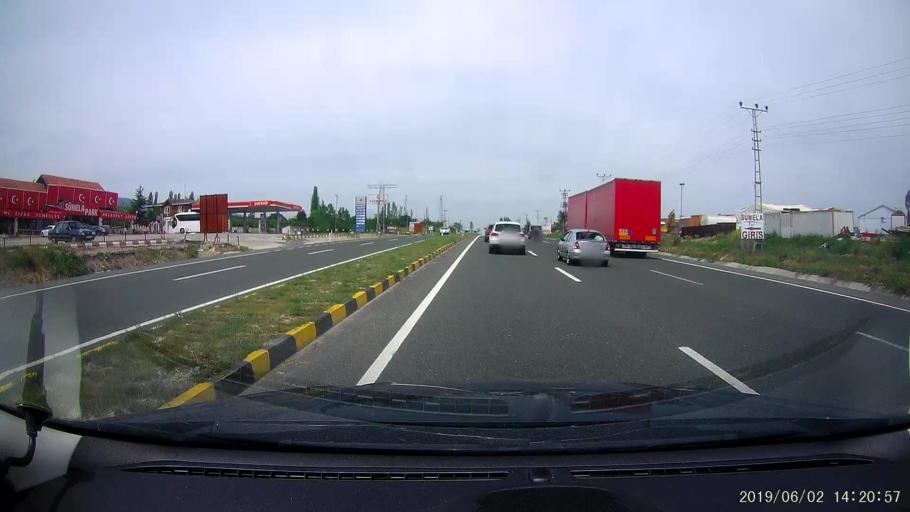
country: TR
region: Kastamonu
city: Tosya
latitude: 40.9742
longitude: 33.9980
